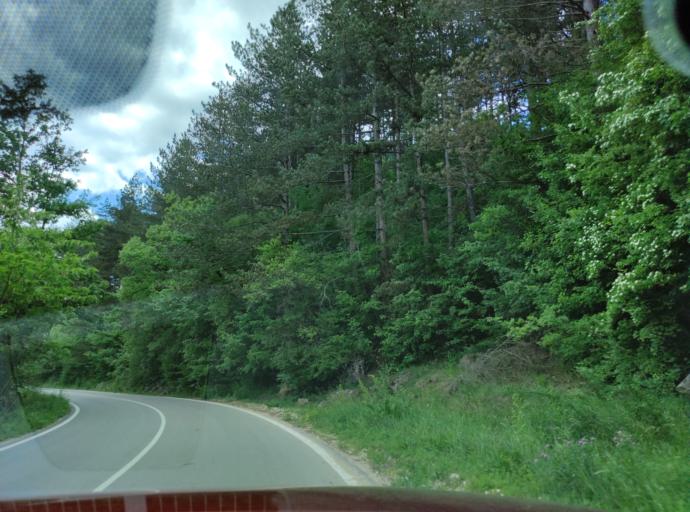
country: BG
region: Montana
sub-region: Obshtina Chiprovtsi
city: Chiprovtsi
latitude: 43.4654
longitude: 22.8796
